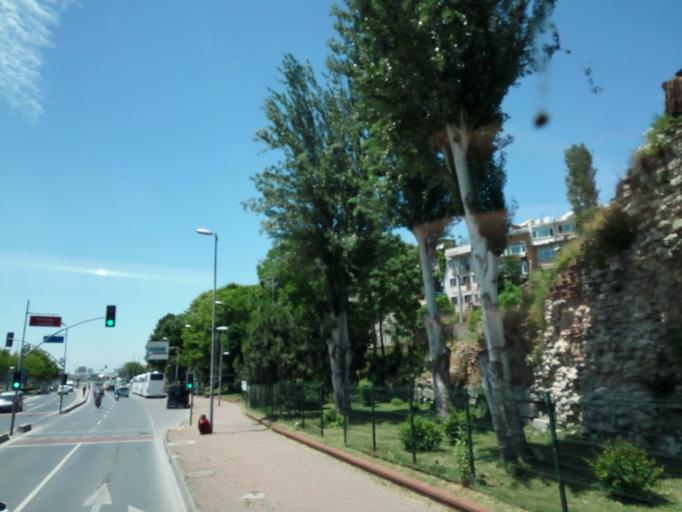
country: TR
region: Istanbul
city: Eminoenue
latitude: 41.0022
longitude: 28.9757
